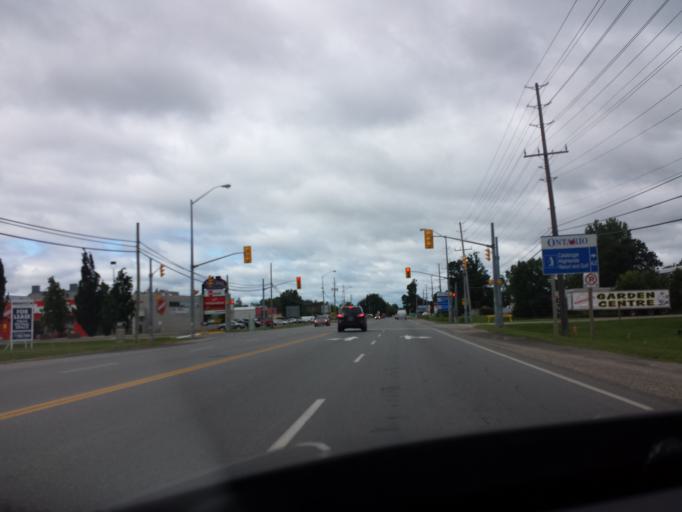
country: CA
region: Ontario
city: Perth
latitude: 44.9092
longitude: -76.2656
